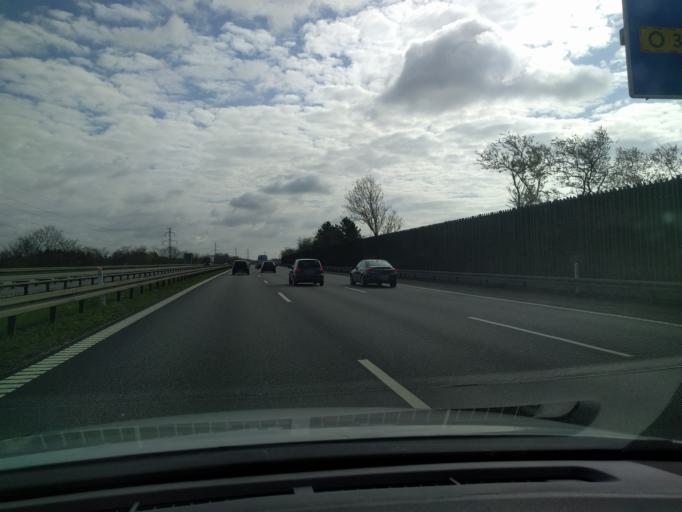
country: DK
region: Capital Region
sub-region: Vallensbaek Kommune
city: Vallensbaek
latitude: 55.6265
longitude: 12.3666
